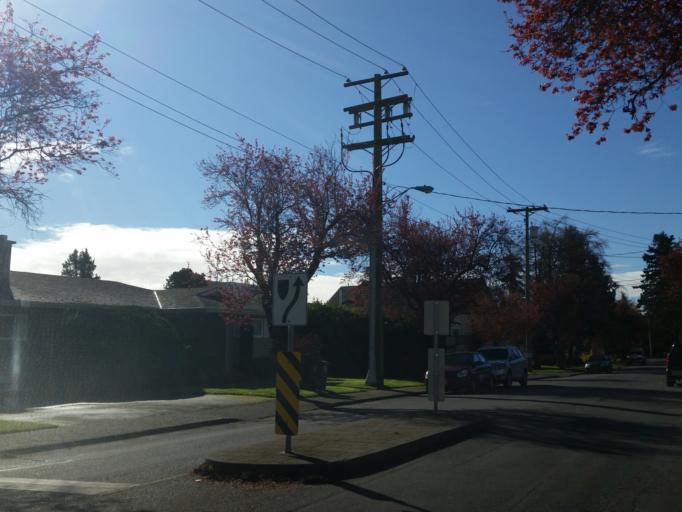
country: CA
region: British Columbia
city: Victoria
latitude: 48.4328
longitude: -123.3936
